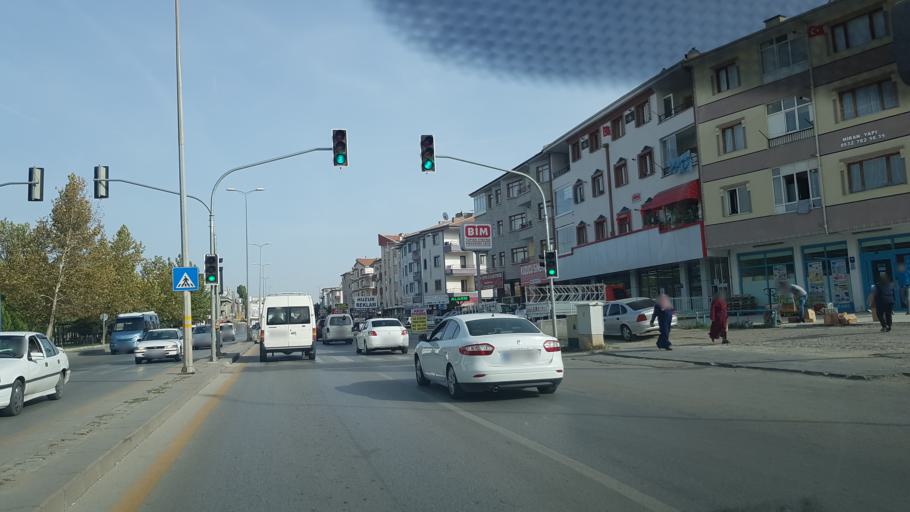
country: TR
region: Ankara
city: Etimesgut
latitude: 39.9550
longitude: 32.6308
